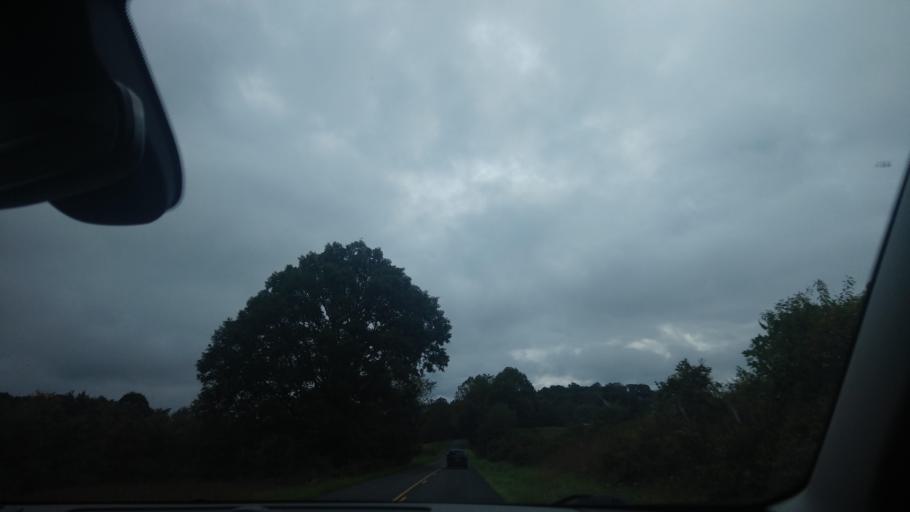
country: US
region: Virginia
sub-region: Carroll County
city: Cana
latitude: 36.6695
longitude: -80.6126
